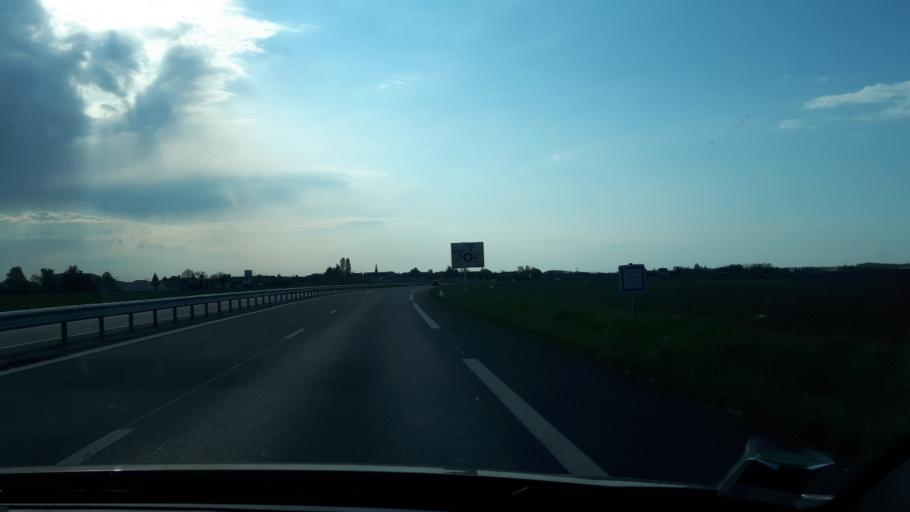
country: FR
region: Centre
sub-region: Departement du Loir-et-Cher
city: Saint-Sulpice-de-Pommeray
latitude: 47.6754
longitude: 1.2277
